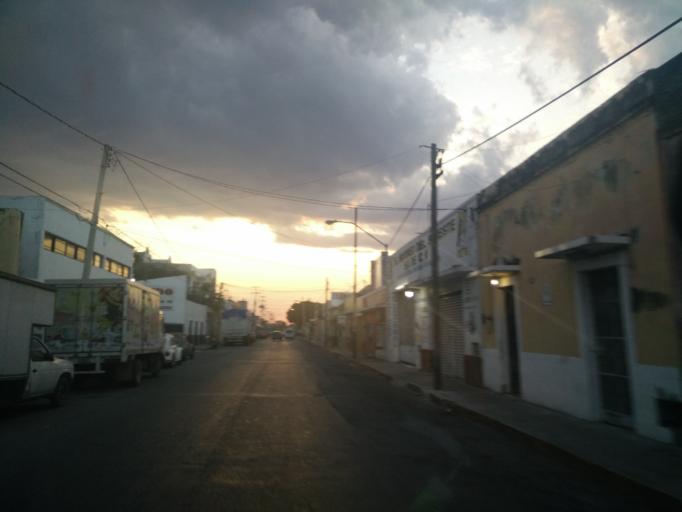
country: MX
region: Yucatan
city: Merida
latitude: 20.9632
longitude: -89.6310
